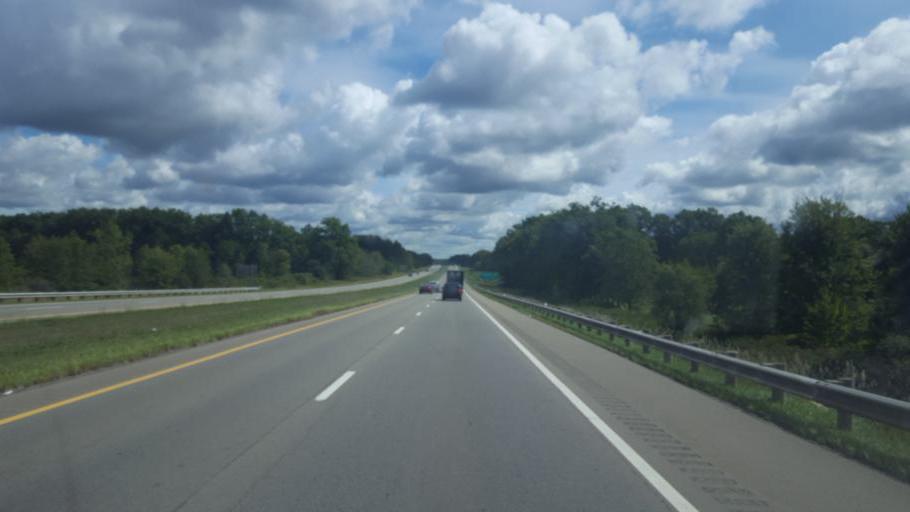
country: US
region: Ohio
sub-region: Lorain County
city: Elyria
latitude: 41.3222
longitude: -82.1013
